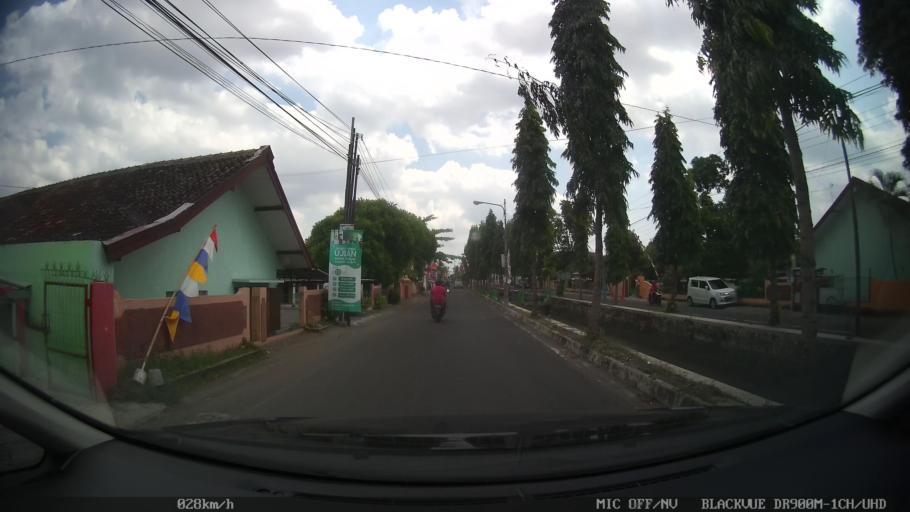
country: ID
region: Daerah Istimewa Yogyakarta
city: Yogyakarta
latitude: -7.7616
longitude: 110.3650
